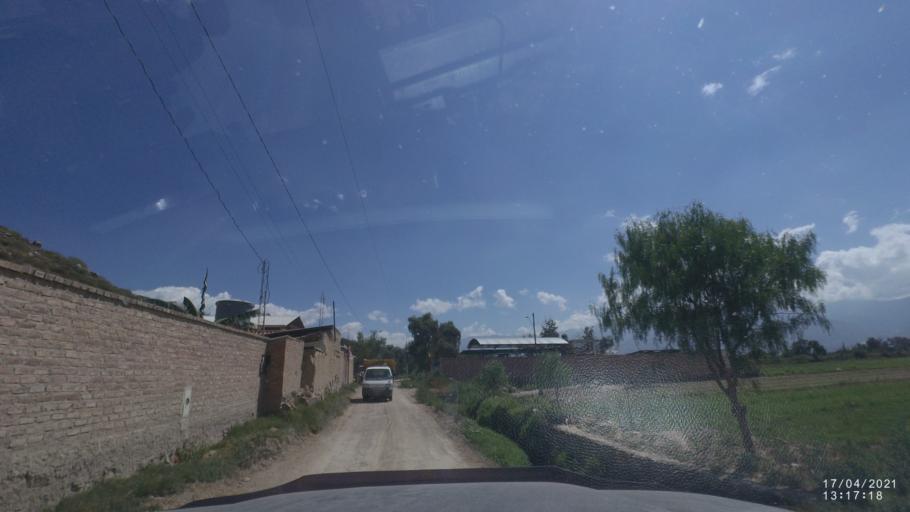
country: BO
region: Cochabamba
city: Cochabamba
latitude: -17.4159
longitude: -66.2413
